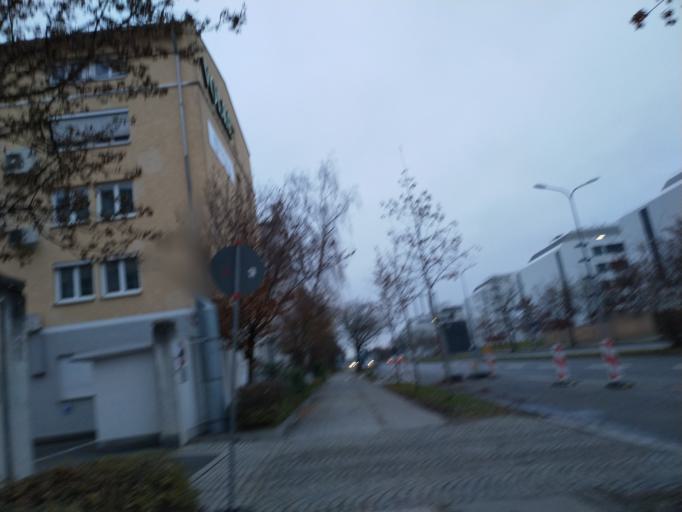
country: DE
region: Bavaria
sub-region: Upper Bavaria
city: Oberschleissheim
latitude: 48.1940
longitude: 11.5649
